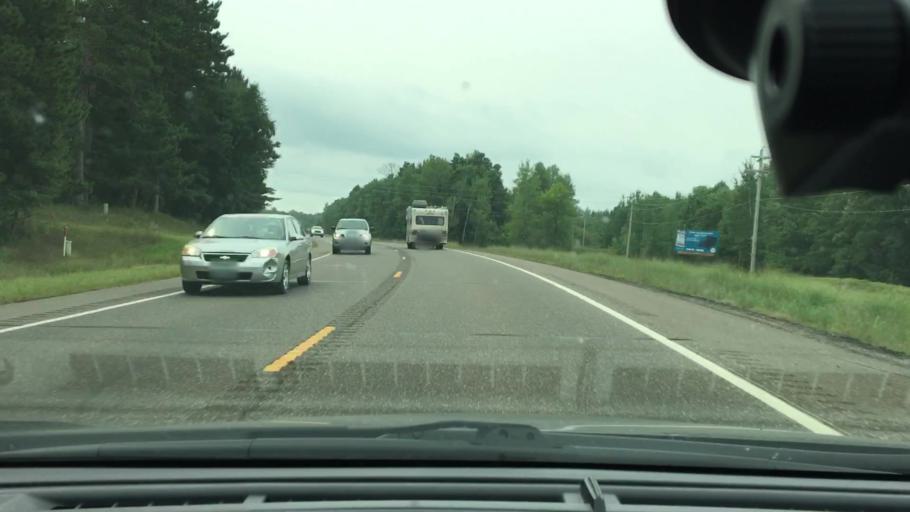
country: US
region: Minnesota
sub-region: Crow Wing County
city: Crosby
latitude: 46.4980
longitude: -93.9573
